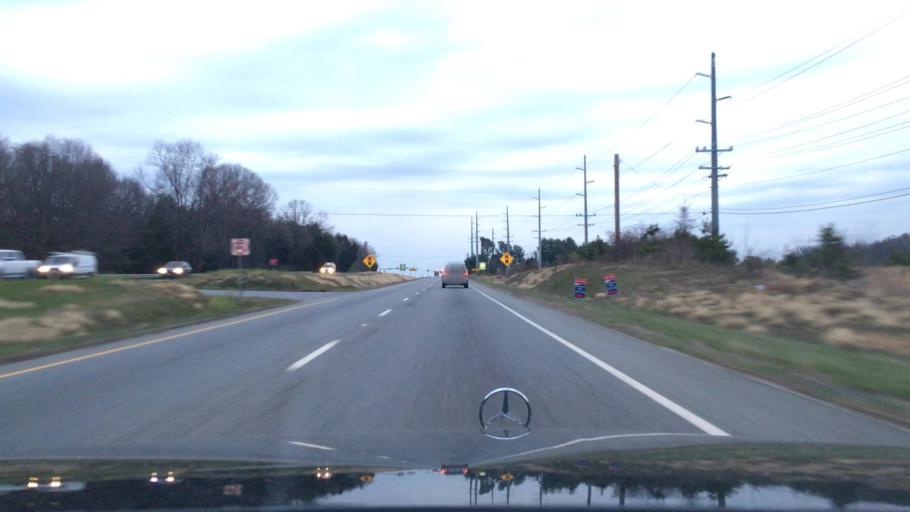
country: US
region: Virginia
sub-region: Greene County
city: Ruckersville
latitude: 38.2034
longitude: -78.3889
